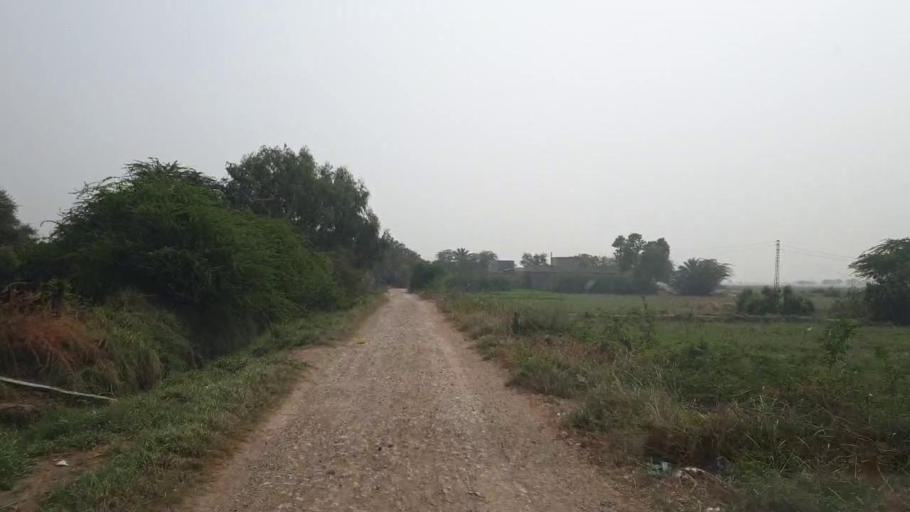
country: PK
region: Sindh
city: Kario
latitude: 24.6503
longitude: 68.6017
